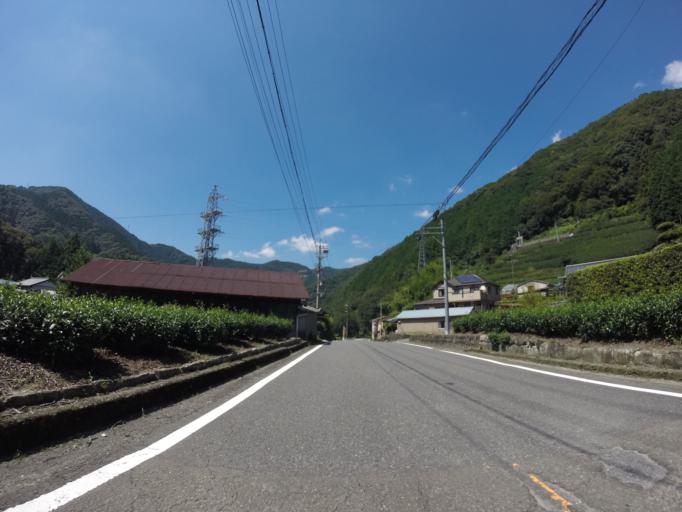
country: JP
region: Shizuoka
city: Shizuoka-shi
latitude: 35.0476
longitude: 138.2513
